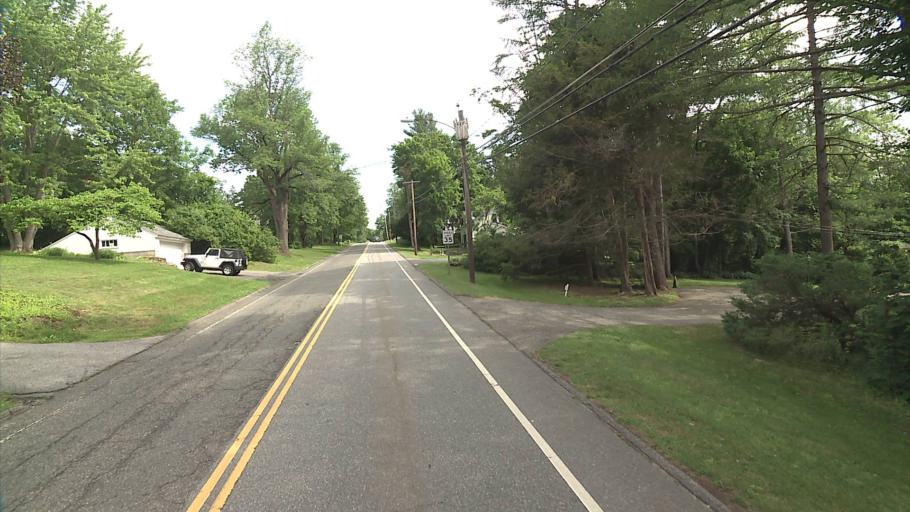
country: US
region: Connecticut
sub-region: Litchfield County
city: Litchfield
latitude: 41.7358
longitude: -73.1865
